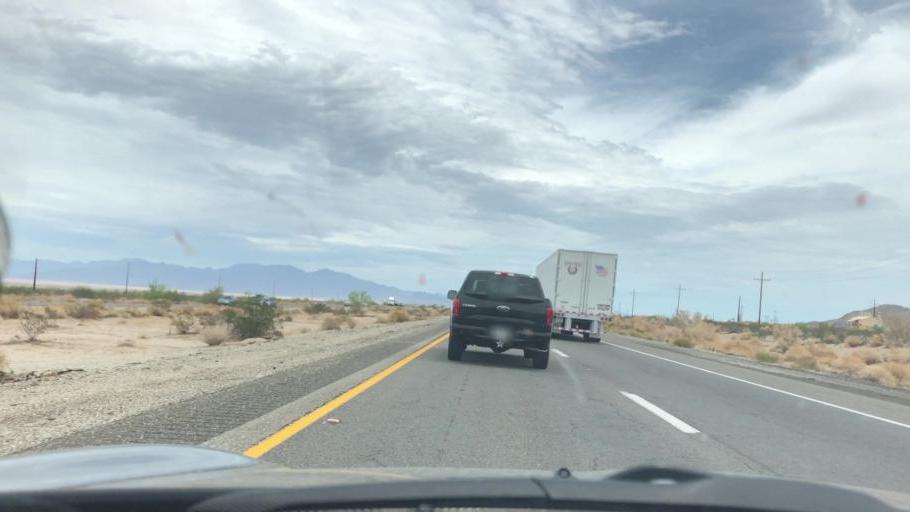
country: US
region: California
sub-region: Imperial County
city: Niland
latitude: 33.7104
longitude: -115.3863
